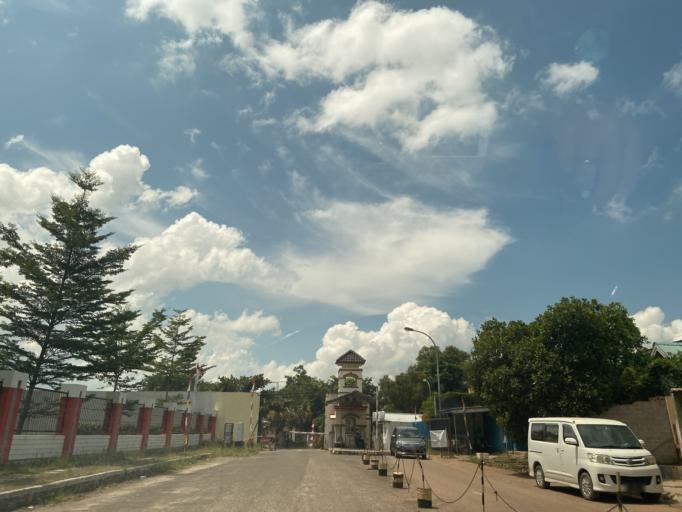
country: SG
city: Singapore
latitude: 1.1127
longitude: 104.0298
